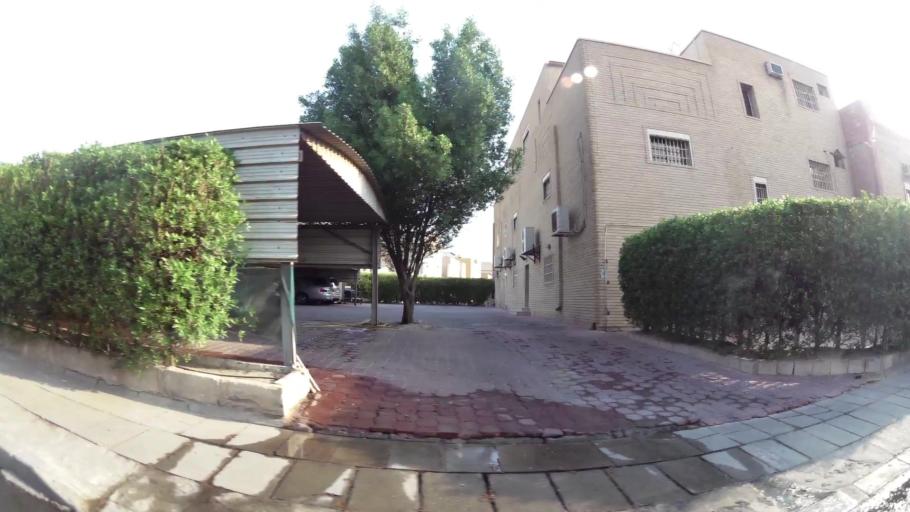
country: KW
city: Bayan
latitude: 29.2969
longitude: 48.0528
